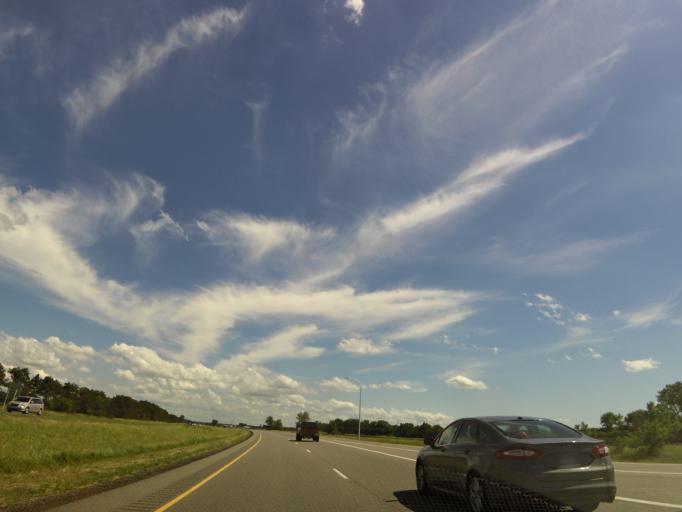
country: US
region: Minnesota
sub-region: Benton County
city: Rice
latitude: 45.7427
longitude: -94.2104
